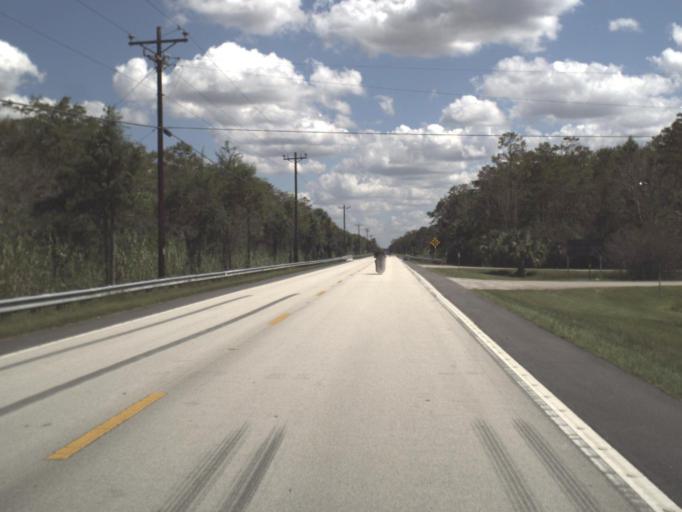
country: US
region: Florida
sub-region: Collier County
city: Marco
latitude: 25.8961
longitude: -81.2820
